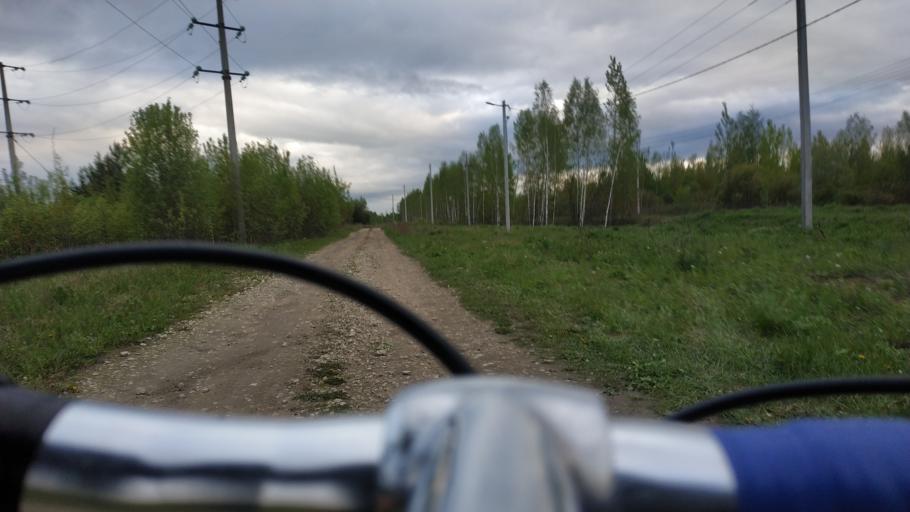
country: RU
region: Moskovskaya
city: Ramenskoye
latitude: 55.6031
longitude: 38.2850
